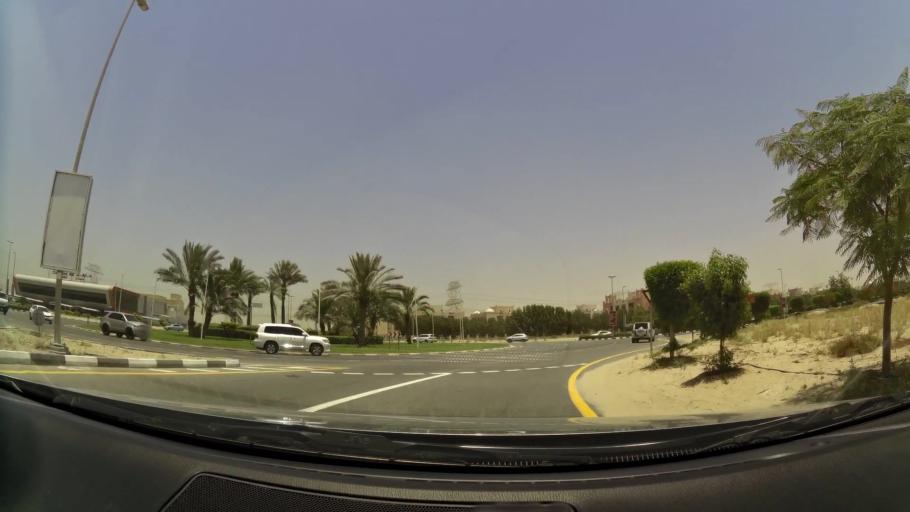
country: AE
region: Dubai
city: Dubai
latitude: 24.9965
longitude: 55.1757
